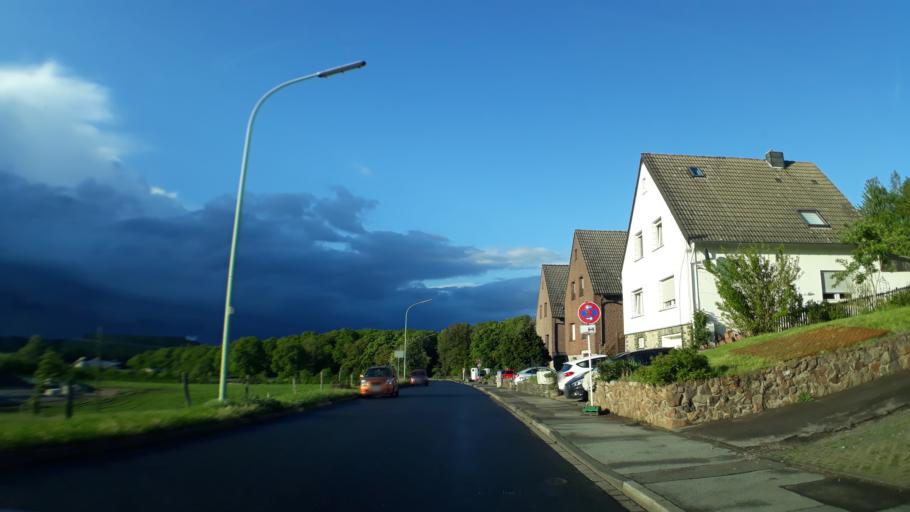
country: DE
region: North Rhine-Westphalia
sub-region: Regierungsbezirk Koln
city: Eschweiler
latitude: 50.7744
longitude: 6.3094
